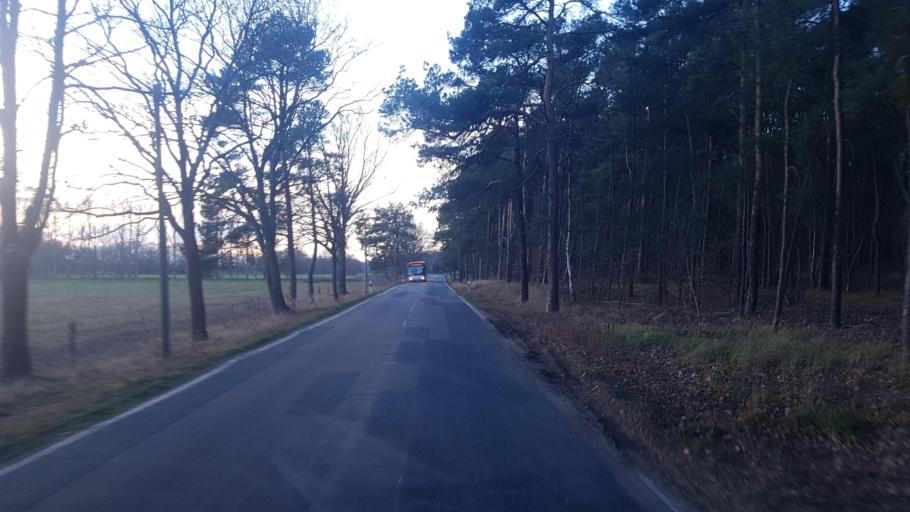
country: DE
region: Brandenburg
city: Briesen
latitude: 51.8518
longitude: 14.2386
